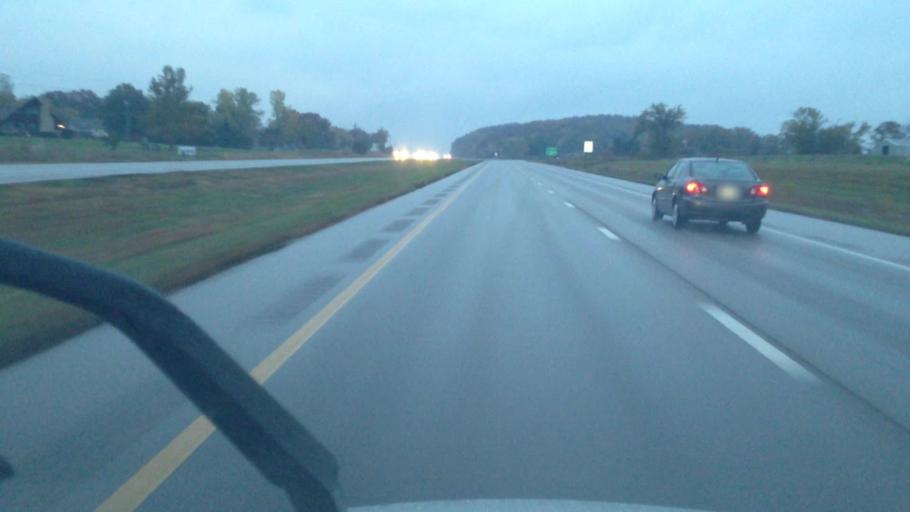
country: US
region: Kansas
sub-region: Douglas County
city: Lawrence
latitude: 38.8974
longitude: -95.2606
